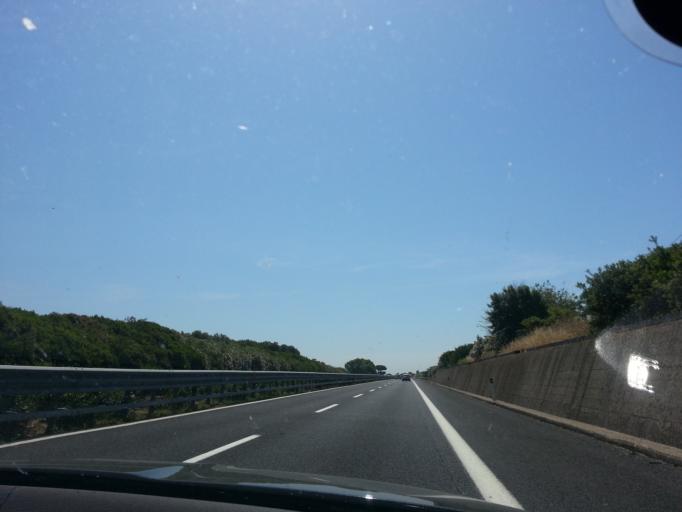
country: IT
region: Latium
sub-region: Citta metropolitana di Roma Capitale
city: Marina di Cerveteri
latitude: 41.9921
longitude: 12.0577
